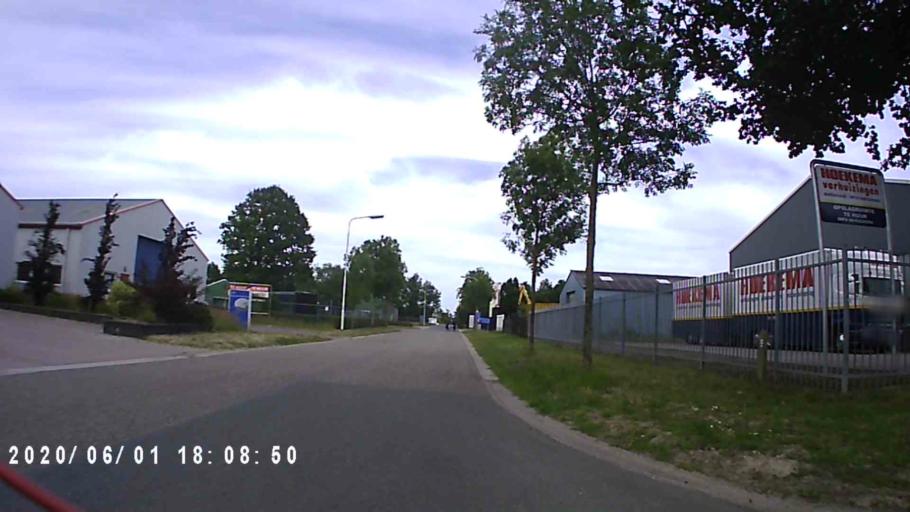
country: NL
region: Friesland
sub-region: Gemeente Tytsjerksteradiel
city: Sumar
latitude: 53.1820
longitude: 6.0039
